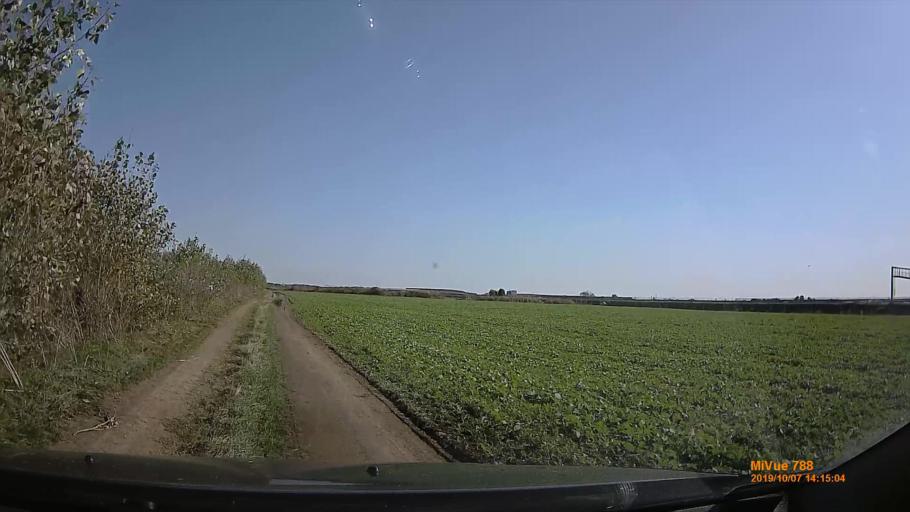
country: HU
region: Jasz-Nagykun-Szolnok
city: Kunszentmarton
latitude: 46.8783
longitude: 20.2533
